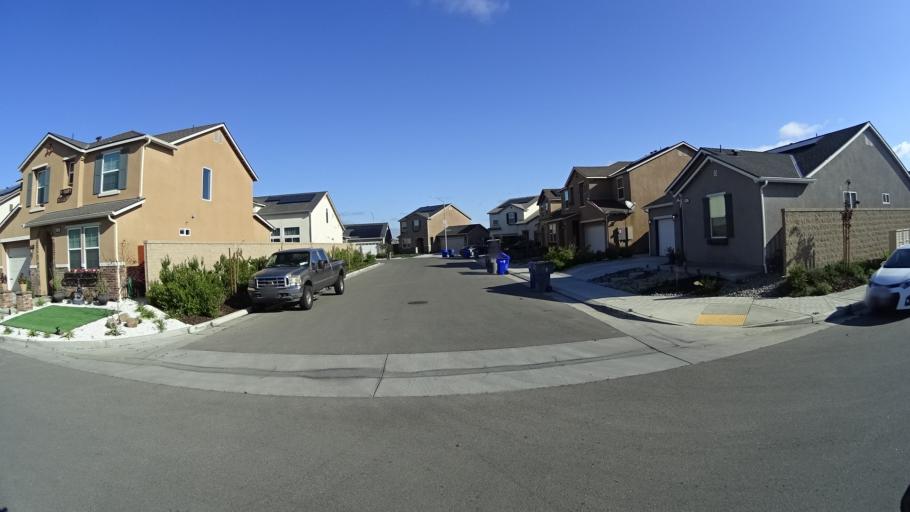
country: US
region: California
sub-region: Fresno County
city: West Park
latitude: 36.7998
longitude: -119.9036
